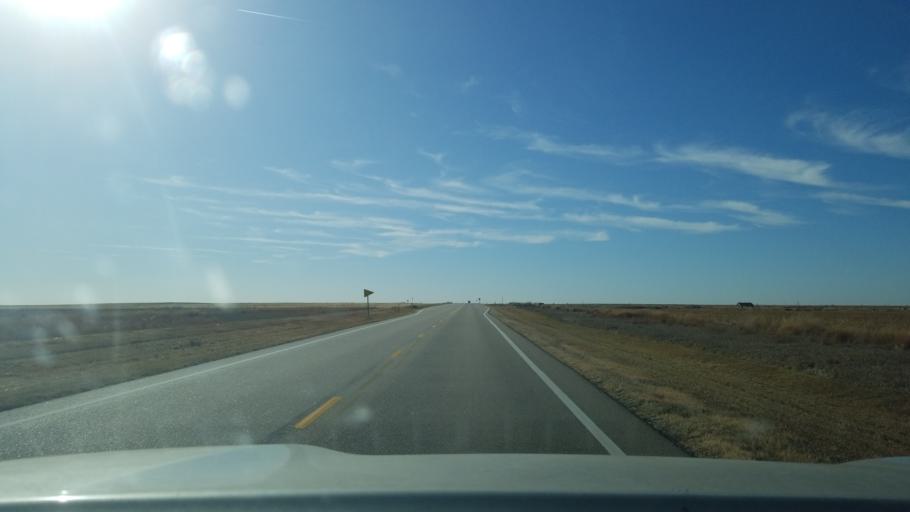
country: US
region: Kansas
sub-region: Ness County
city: Ness City
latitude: 38.3510
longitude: -99.8979
